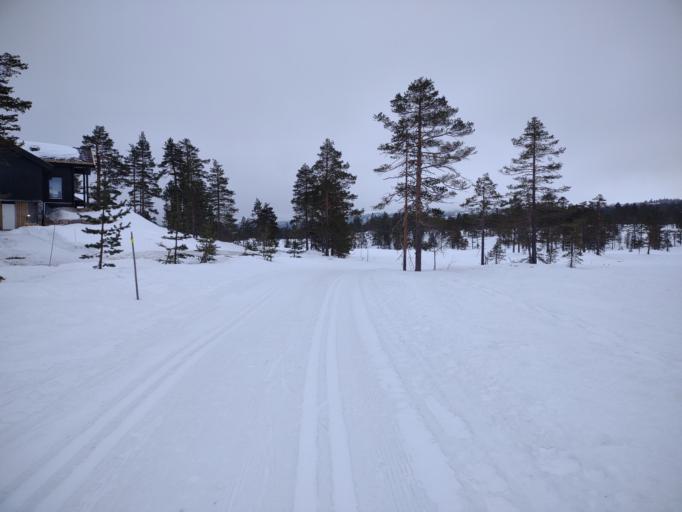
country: NO
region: Buskerud
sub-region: Flesberg
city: Lampeland
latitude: 59.7928
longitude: 9.4414
